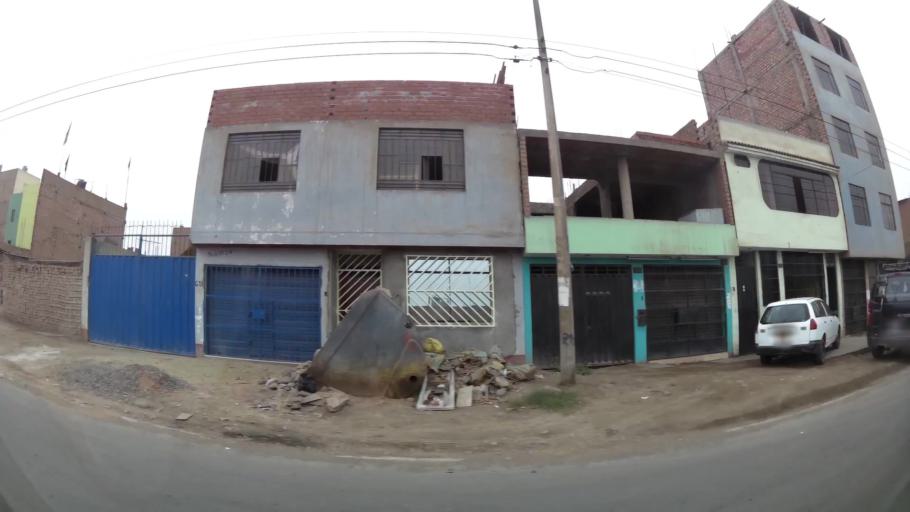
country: PE
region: Lima
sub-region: Lima
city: Urb. Santo Domingo
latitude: -11.8827
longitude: -77.0376
